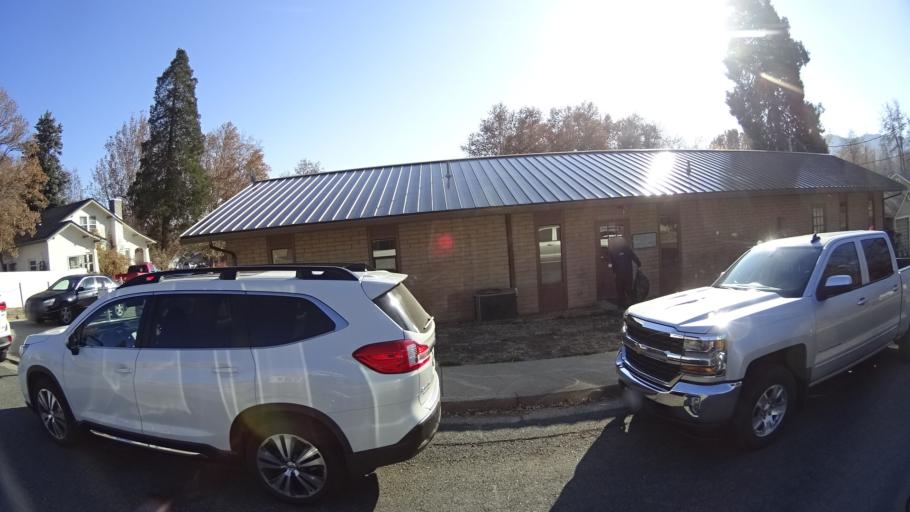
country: US
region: California
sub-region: Siskiyou County
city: Yreka
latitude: 41.7376
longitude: -122.6348
